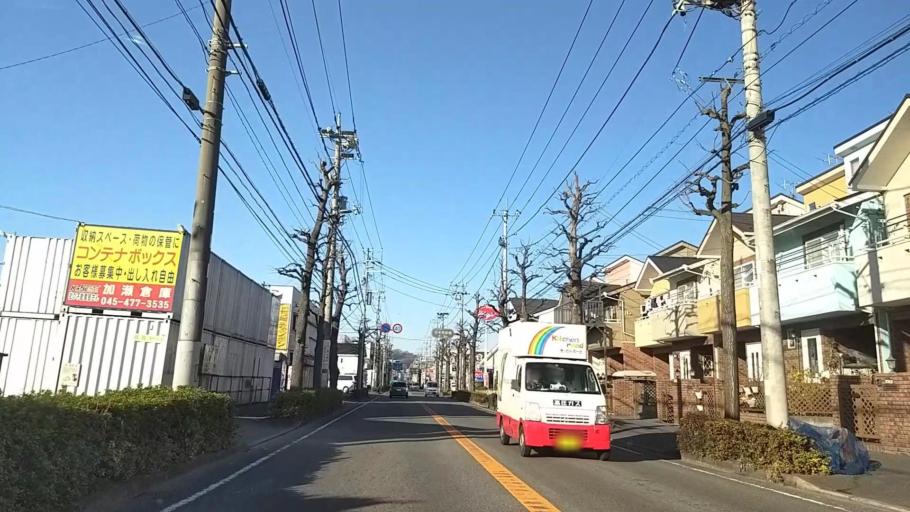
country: JP
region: Tokyo
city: Chofugaoka
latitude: 35.6119
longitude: 139.5795
